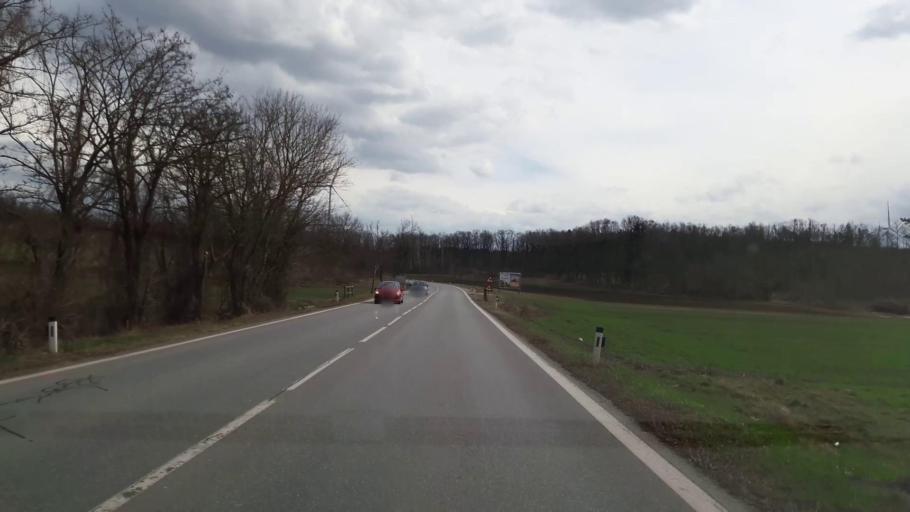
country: AT
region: Lower Austria
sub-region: Politischer Bezirk Mistelbach
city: Mistelbach
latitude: 48.5415
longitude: 16.5919
